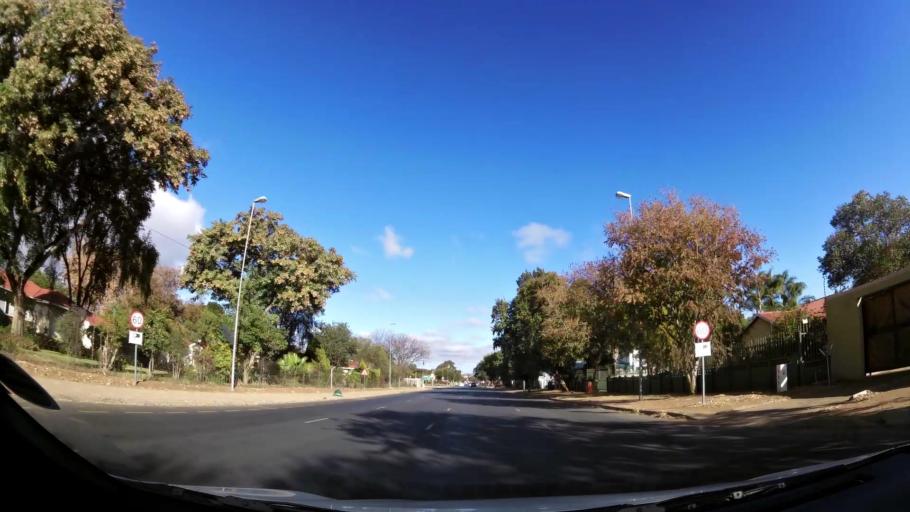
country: ZA
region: Limpopo
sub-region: Capricorn District Municipality
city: Polokwane
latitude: -23.9186
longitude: 29.4632
